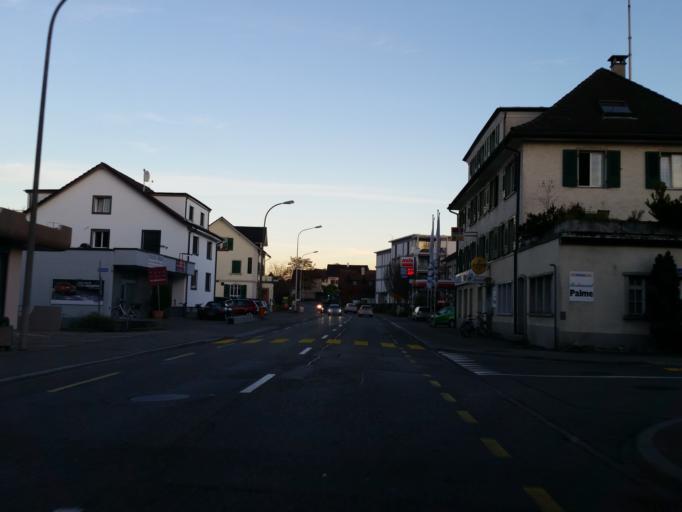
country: CH
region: Thurgau
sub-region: Kreuzlingen District
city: Kreuzlingen
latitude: 47.6411
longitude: 9.1913
